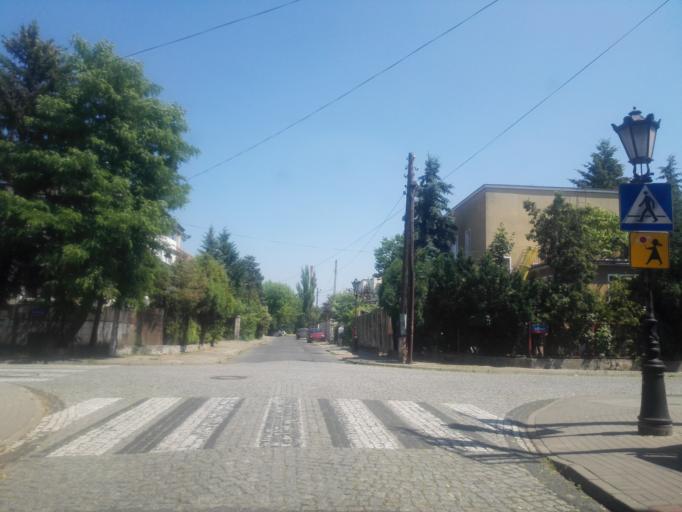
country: PL
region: Masovian Voivodeship
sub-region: Warszawa
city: Wilanow
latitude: 52.1888
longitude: 21.0694
